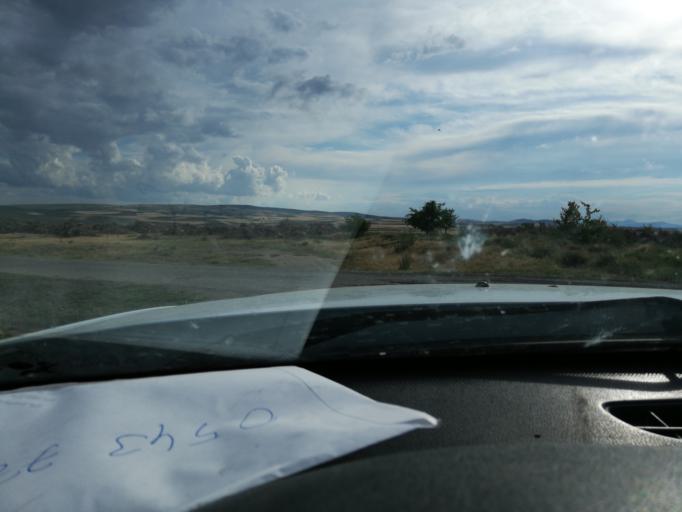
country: TR
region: Kirsehir
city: Kirsehir
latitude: 39.0032
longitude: 34.1197
